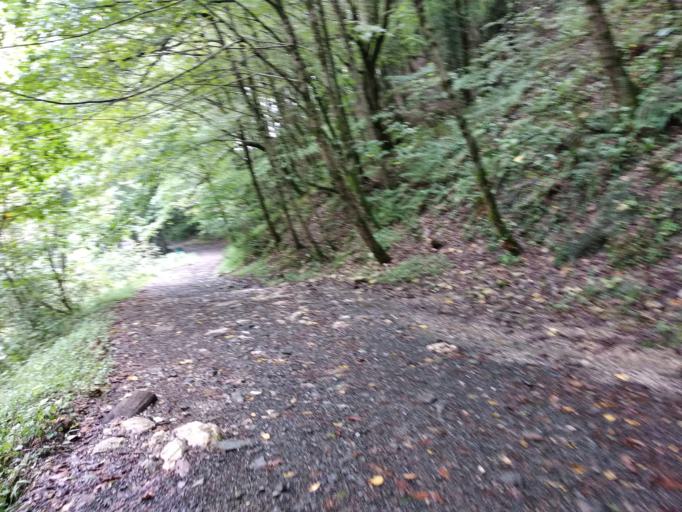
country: RU
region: Krasnodarskiy
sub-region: Sochi City
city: Sochi
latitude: 43.6385
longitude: 39.8108
